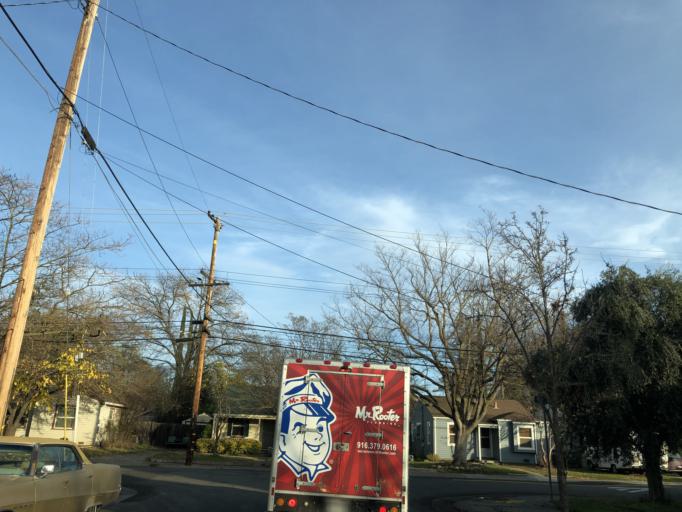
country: US
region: California
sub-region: Sacramento County
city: Parkway
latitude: 38.5508
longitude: -121.4397
